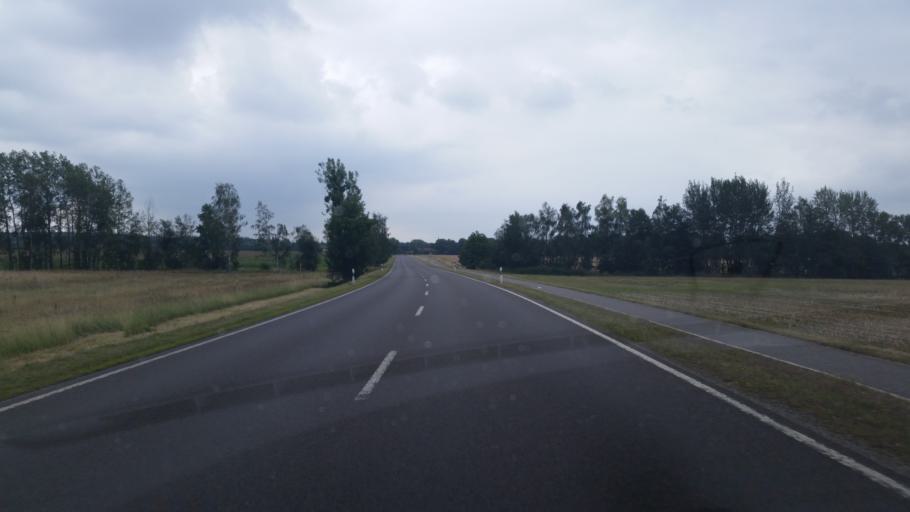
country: DE
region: Brandenburg
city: Hohenbocka
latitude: 51.4721
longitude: 14.0678
